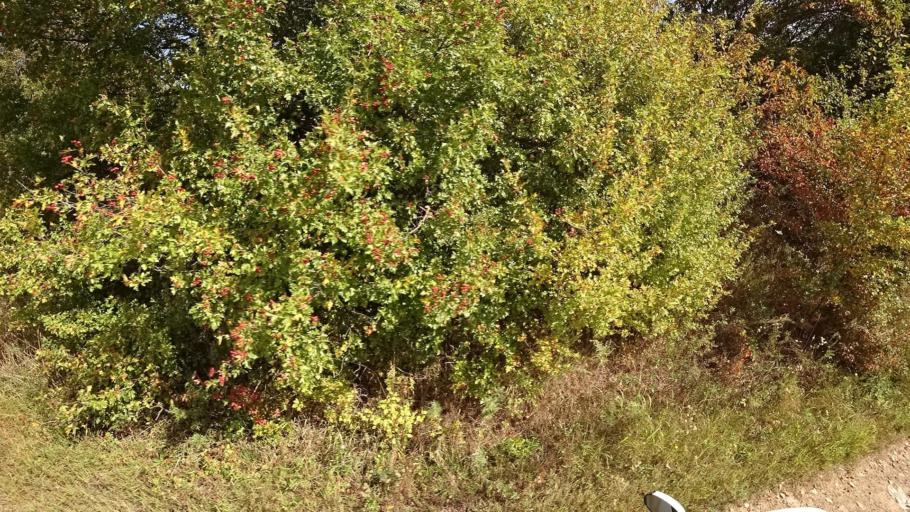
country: RU
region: Primorskiy
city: Yakovlevka
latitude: 44.7061
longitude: 133.6418
